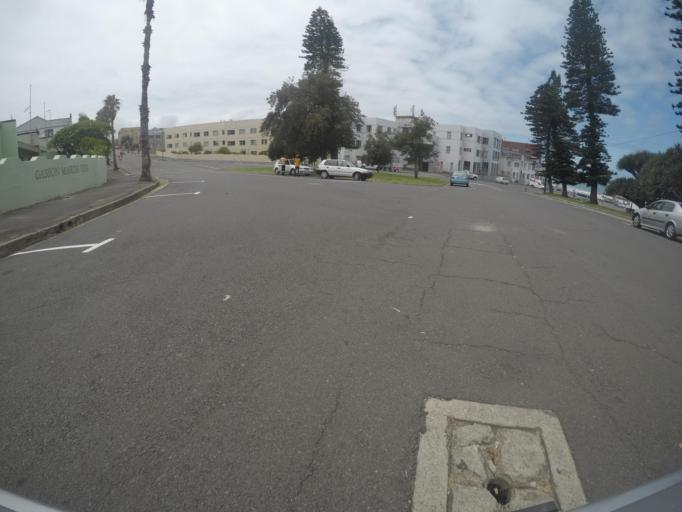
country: ZA
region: Eastern Cape
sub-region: Buffalo City Metropolitan Municipality
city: East London
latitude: -33.0214
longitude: 27.9164
